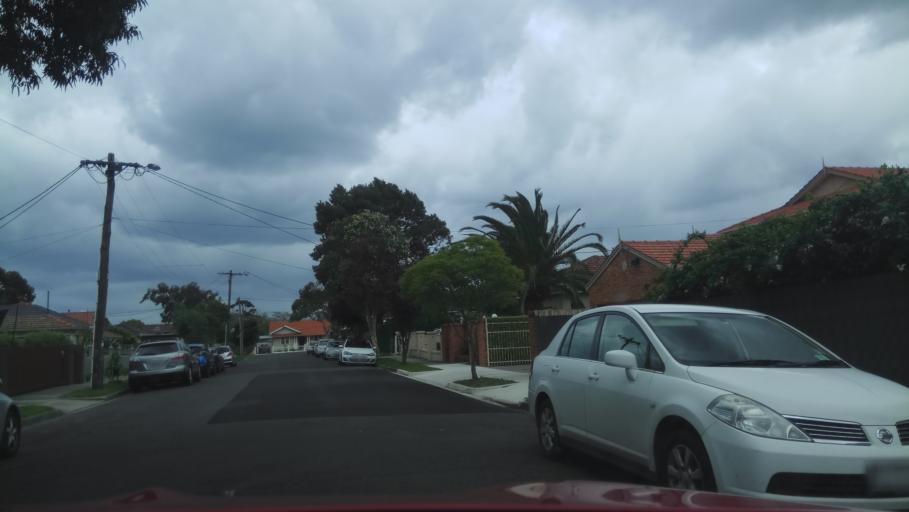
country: AU
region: Victoria
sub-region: Hobsons Bay
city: Newport
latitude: -37.8450
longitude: 144.8900
